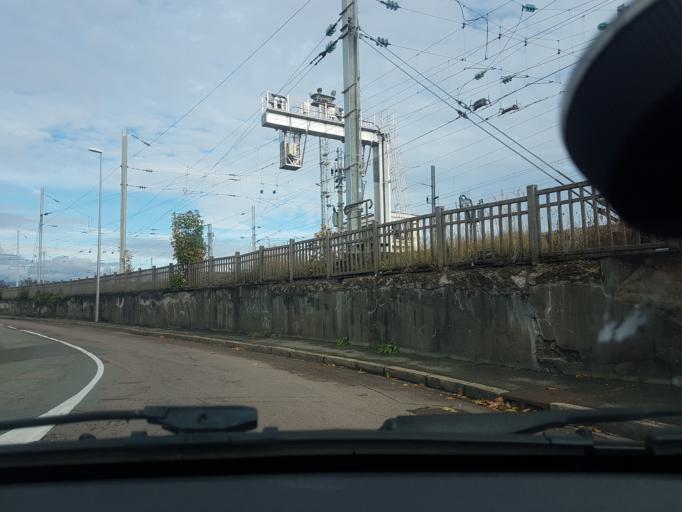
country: FR
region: Franche-Comte
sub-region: Territoire de Belfort
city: Belfort
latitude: 47.6266
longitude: 6.8547
